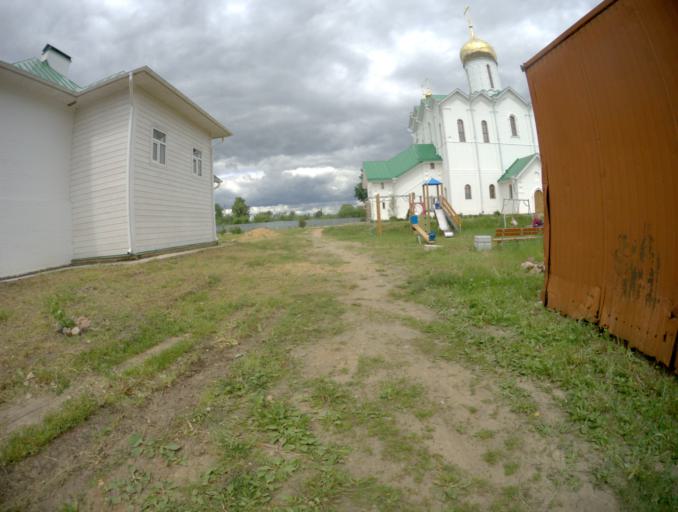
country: RU
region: Ivanovo
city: Savino
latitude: 56.5894
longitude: 41.2099
